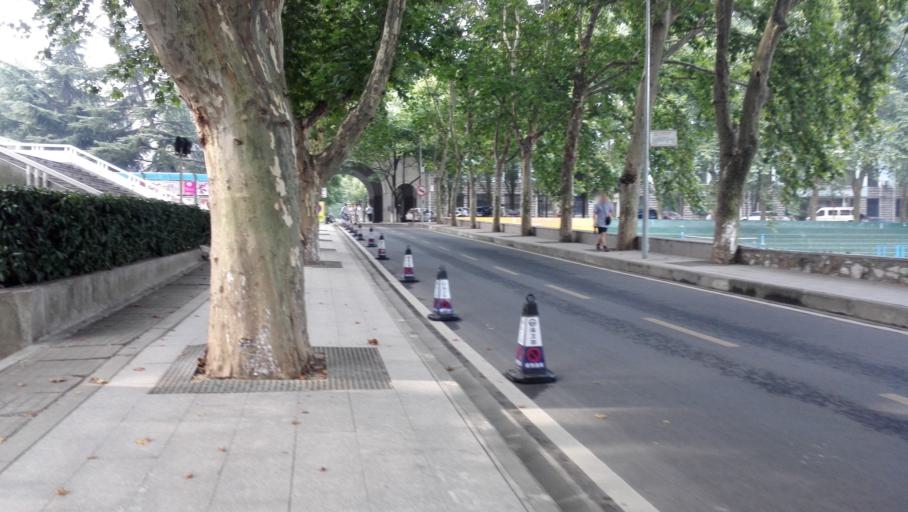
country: CN
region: Hubei
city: Shizishan
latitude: 30.5298
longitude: 114.3564
